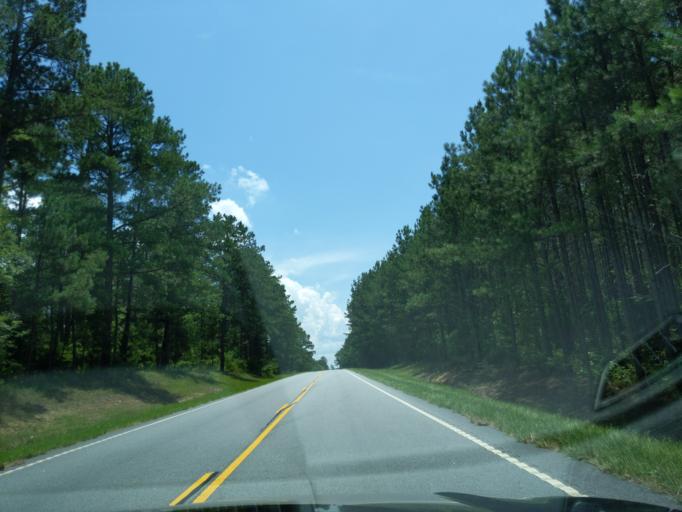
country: US
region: South Carolina
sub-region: Greenwood County
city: Ninety Six
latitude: 33.9666
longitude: -82.0463
